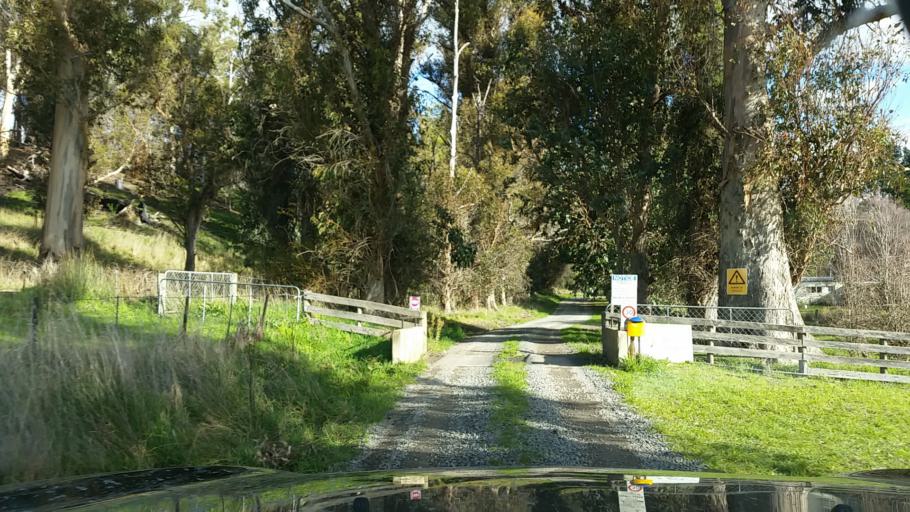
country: NZ
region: Marlborough
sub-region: Marlborough District
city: Blenheim
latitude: -41.7762
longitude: 173.8527
